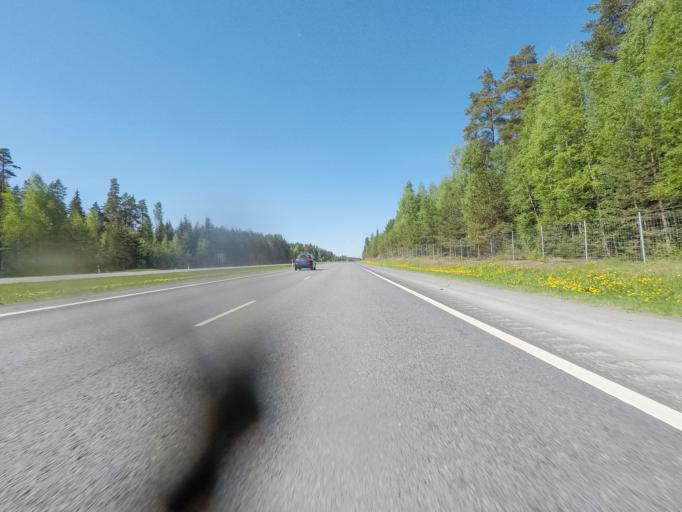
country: FI
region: Haeme
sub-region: Haemeenlinna
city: Kalvola
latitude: 61.1058
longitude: 24.1495
